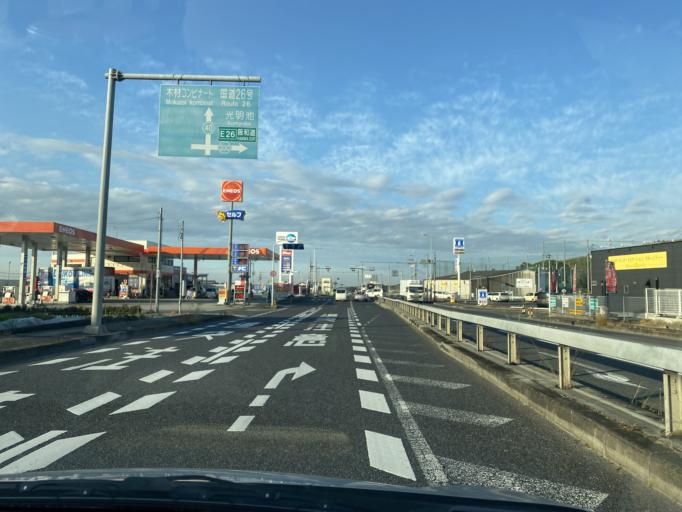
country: JP
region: Osaka
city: Izumi
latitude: 34.4367
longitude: 135.4395
